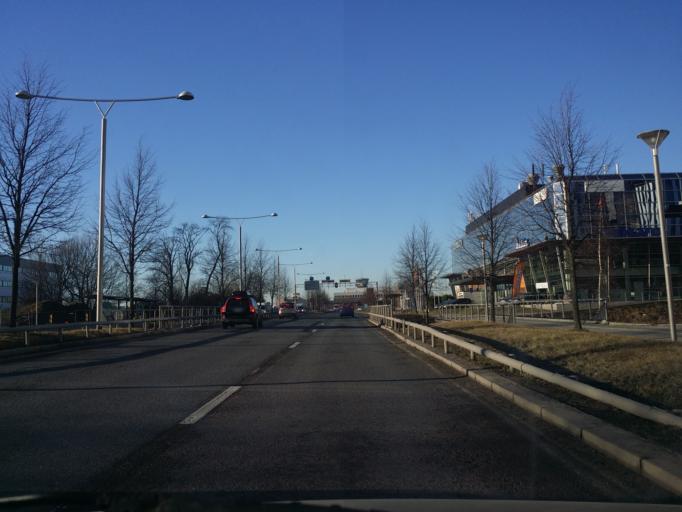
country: NO
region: Akershus
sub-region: Baerum
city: Lysaker
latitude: 59.9039
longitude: 10.6278
